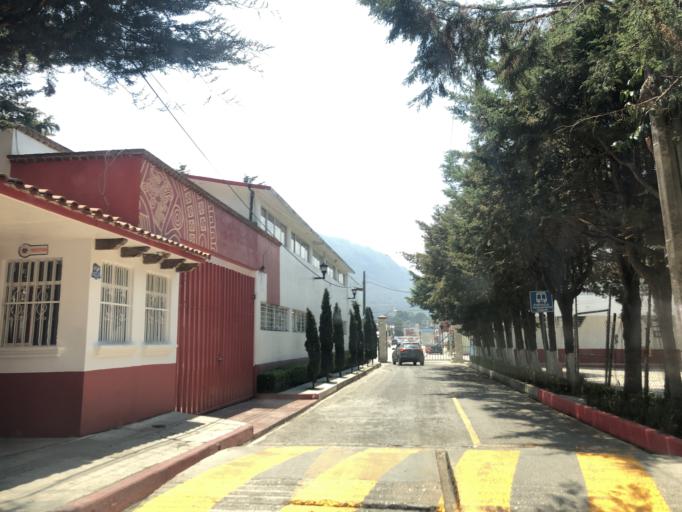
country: MX
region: Chiapas
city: San Cristobal de las Casas
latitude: 16.7165
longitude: -92.6443
